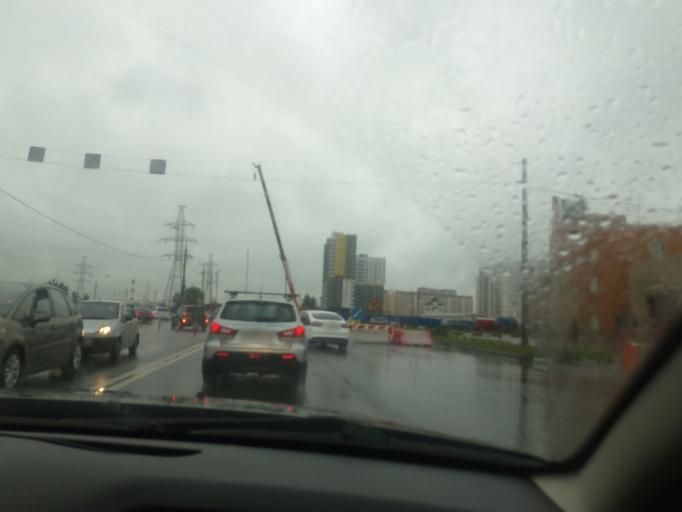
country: RU
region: Moscow
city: Zhulebino
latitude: 55.7093
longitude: 37.8781
